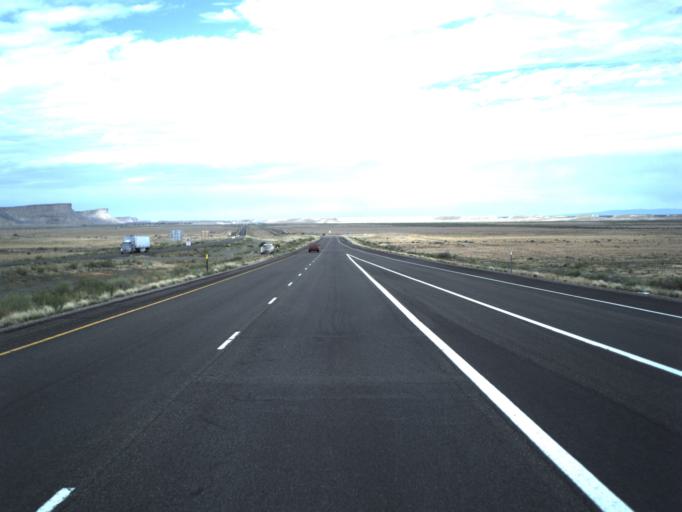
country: US
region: Utah
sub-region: Grand County
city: Moab
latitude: 38.9433
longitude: -109.8091
